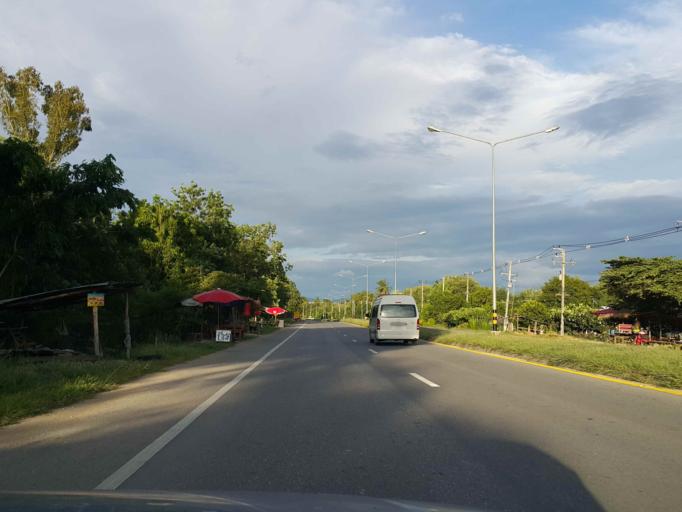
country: TH
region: Sukhothai
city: Ban Dan Lan Hoi
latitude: 16.9219
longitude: 99.3929
